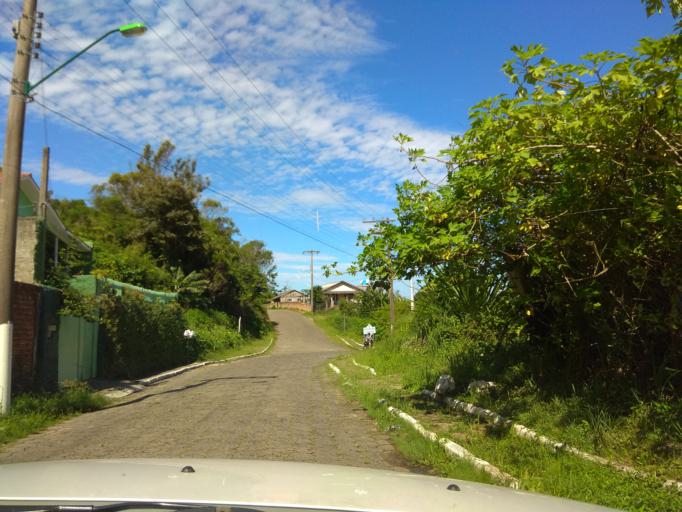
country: BR
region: Santa Catarina
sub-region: Laguna
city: Laguna
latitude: -28.4809
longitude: -48.7745
